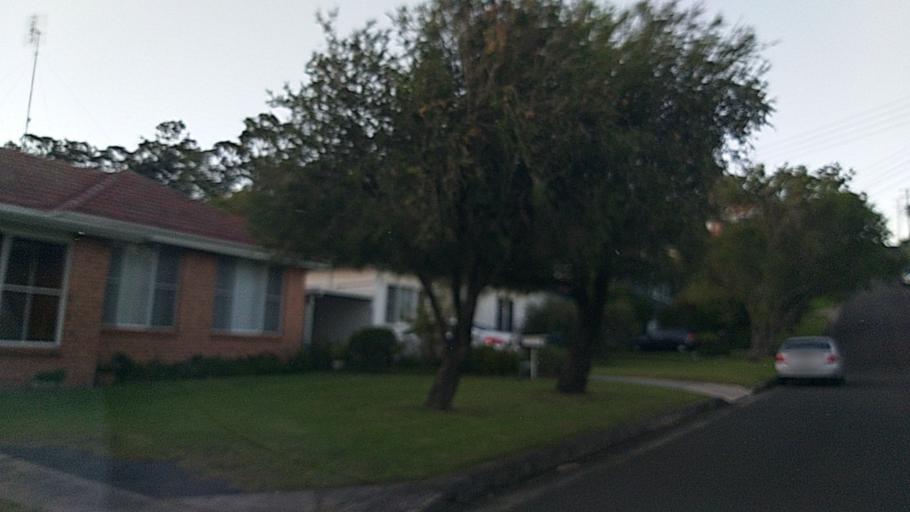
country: AU
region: New South Wales
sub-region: Wollongong
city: West Wollongong
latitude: -34.4222
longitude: 150.8599
